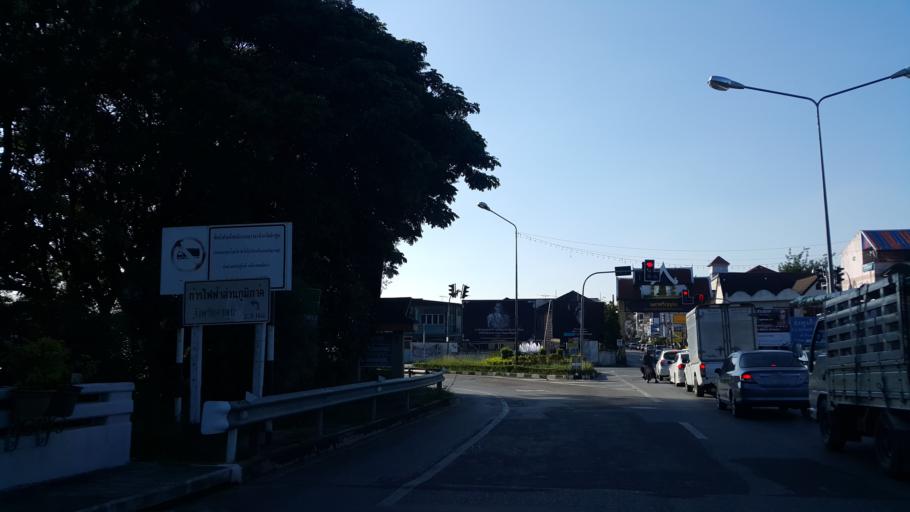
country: TH
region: Lamphun
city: Lamphun
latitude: 18.5742
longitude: 99.0093
